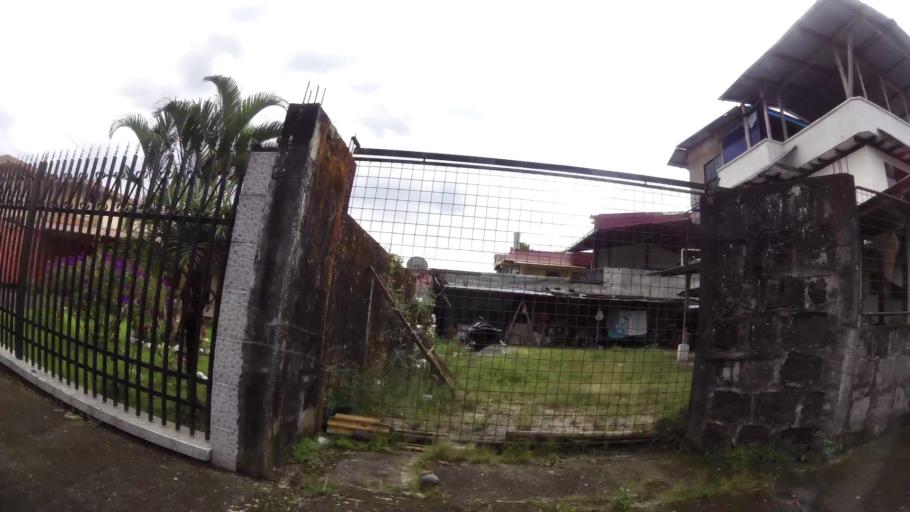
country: EC
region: Pastaza
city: Puyo
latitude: -1.4758
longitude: -78.0016
